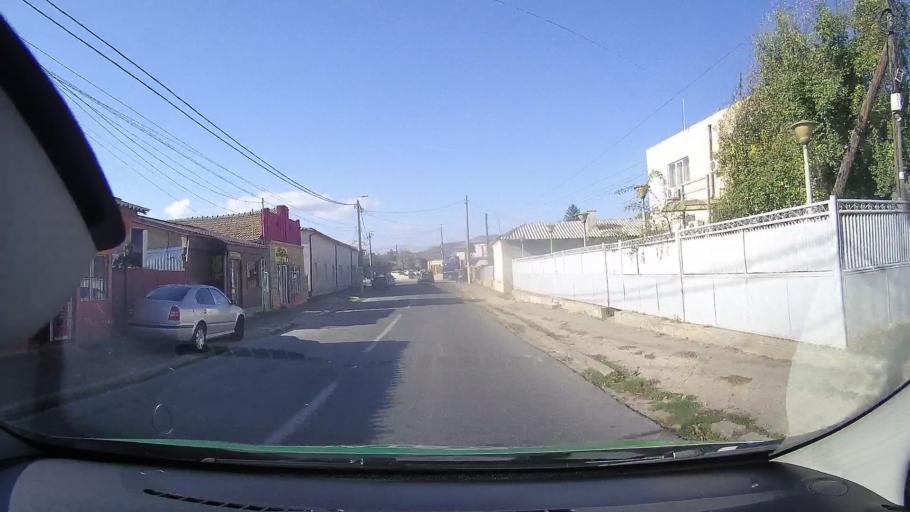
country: RO
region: Tulcea
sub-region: Oras Babadag
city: Babadag
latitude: 44.8930
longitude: 28.7194
